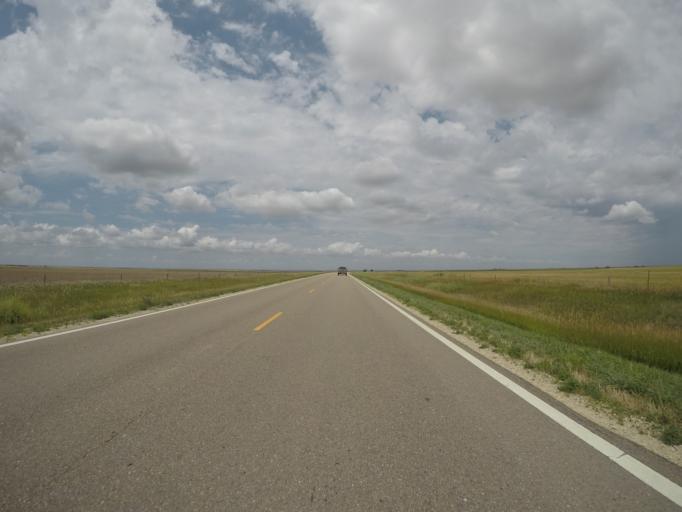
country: US
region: Kansas
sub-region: Rawlins County
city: Atwood
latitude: 39.7289
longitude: -101.0563
